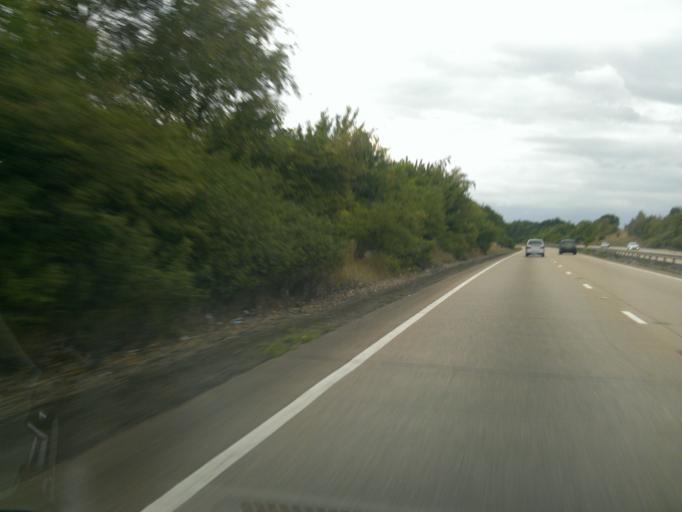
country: GB
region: England
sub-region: Essex
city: Wivenhoe
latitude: 51.9045
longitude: 0.9718
